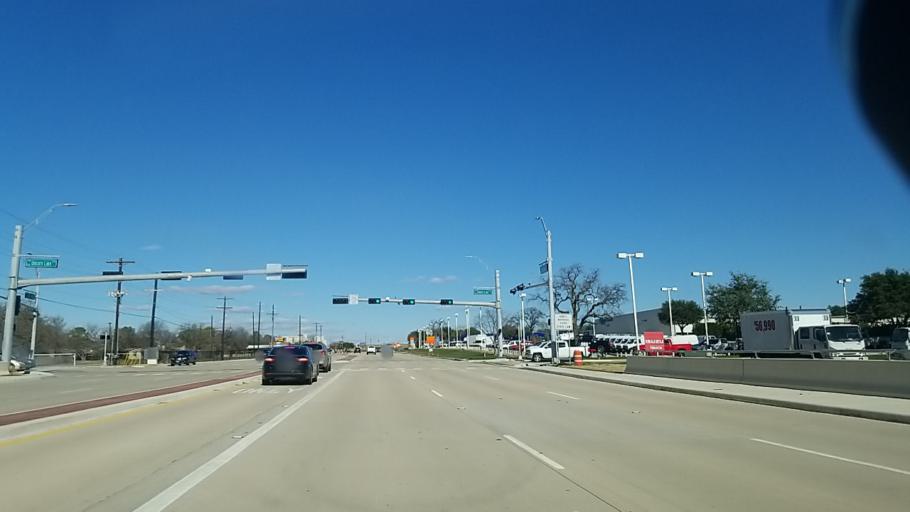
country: US
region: Texas
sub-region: Denton County
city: Corinth
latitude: 33.1690
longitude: -97.0908
